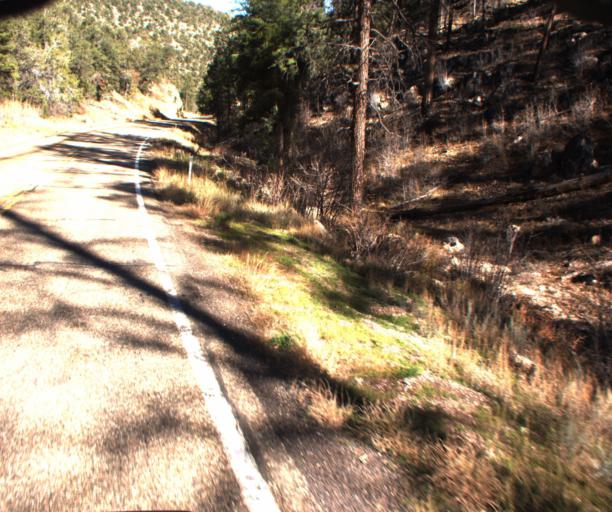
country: US
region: Arizona
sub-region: Coconino County
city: Fredonia
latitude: 36.7342
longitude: -112.1462
